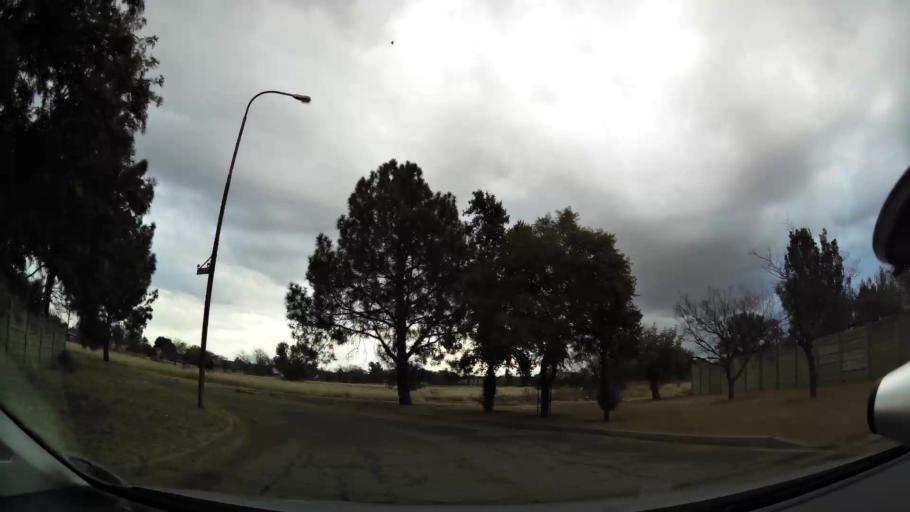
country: ZA
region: Orange Free State
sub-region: Lejweleputswa District Municipality
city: Welkom
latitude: -27.9666
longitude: 26.7244
